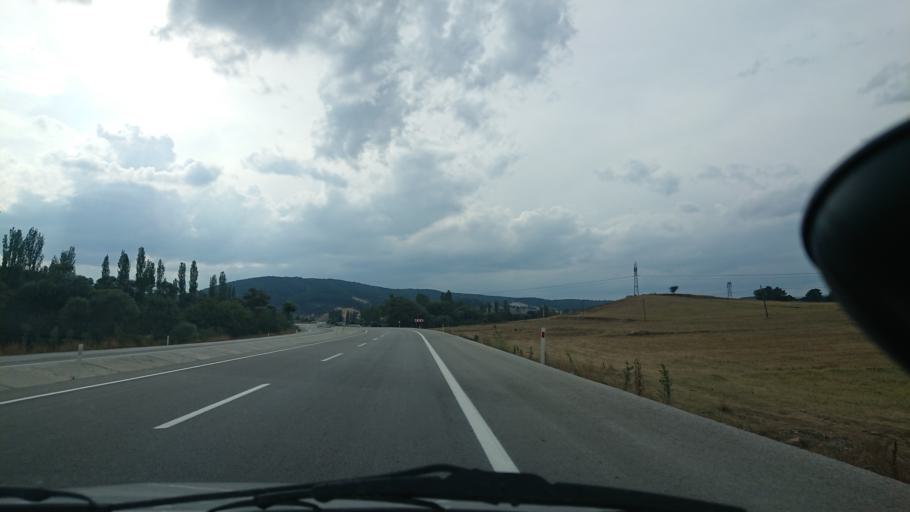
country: TR
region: Kuetahya
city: Cavdarhisar
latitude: 39.1053
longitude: 29.4983
